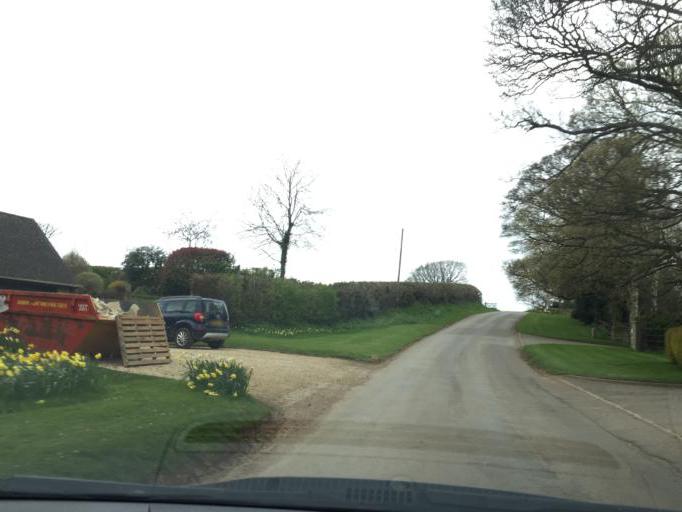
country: GB
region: England
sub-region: Oxfordshire
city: Hanwell
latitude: 52.0944
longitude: -1.3950
